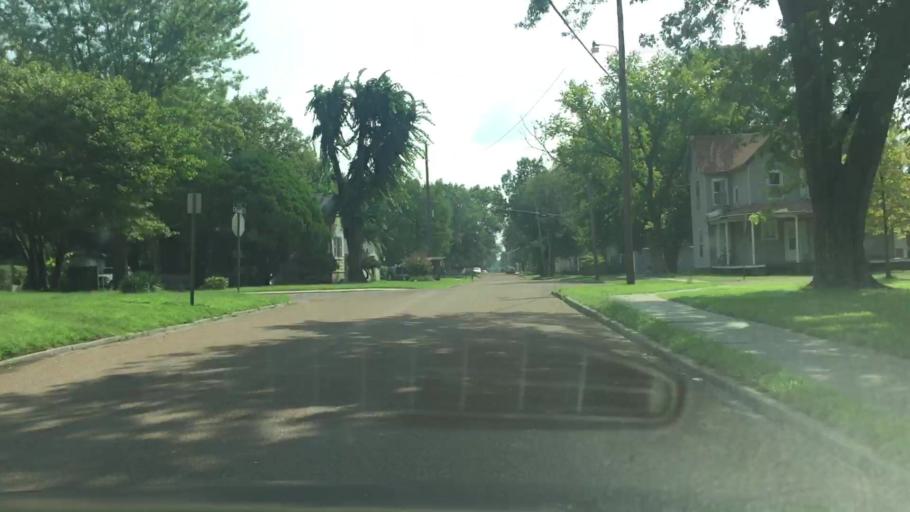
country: US
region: Kansas
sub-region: Allen County
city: Iola
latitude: 37.9199
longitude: -95.3957
